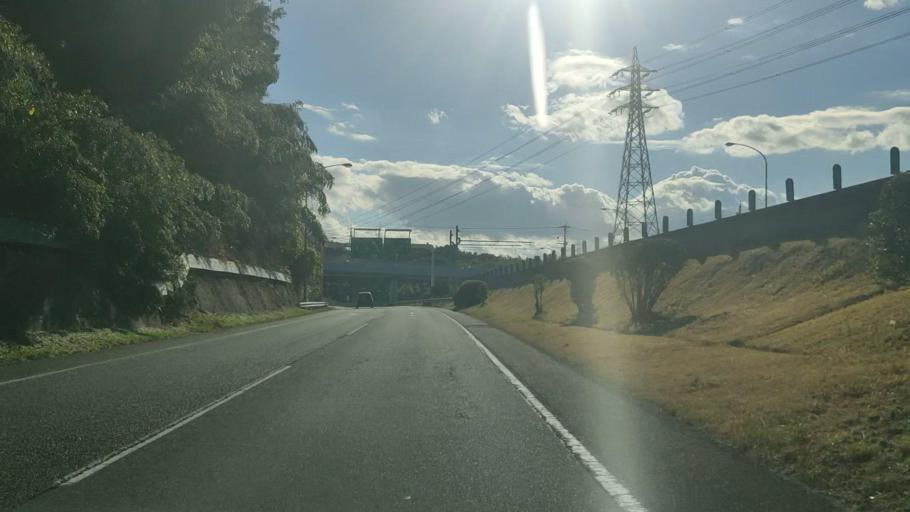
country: JP
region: Fukuoka
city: Kitakyushu
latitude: 33.8440
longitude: 130.7661
